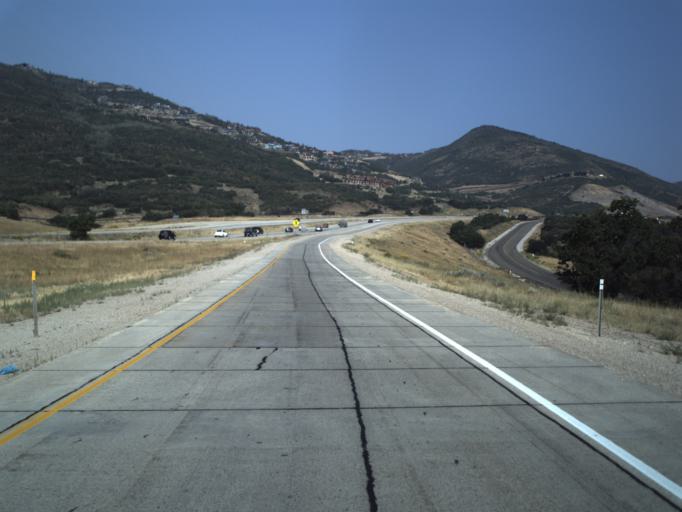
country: US
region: Utah
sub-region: Summit County
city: Park City
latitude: 40.6272
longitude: -111.4413
